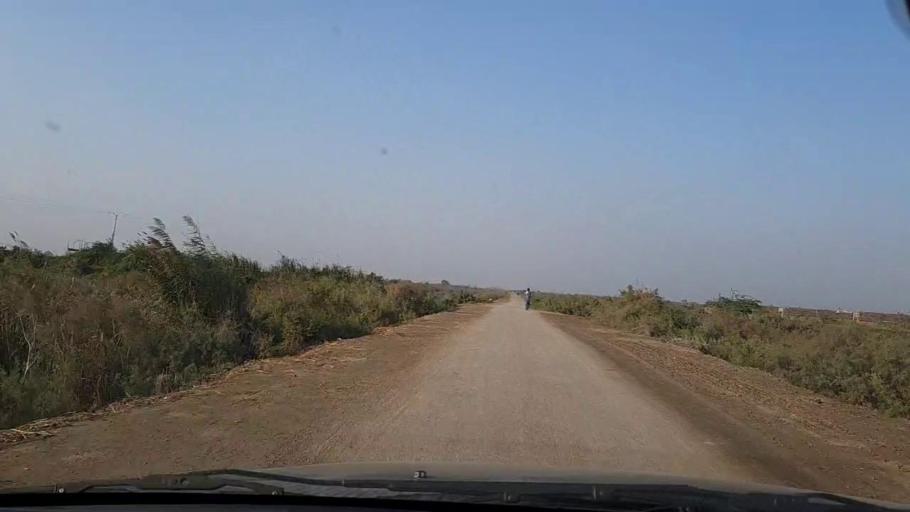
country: PK
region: Sindh
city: Chuhar Jamali
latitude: 24.3077
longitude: 67.7555
